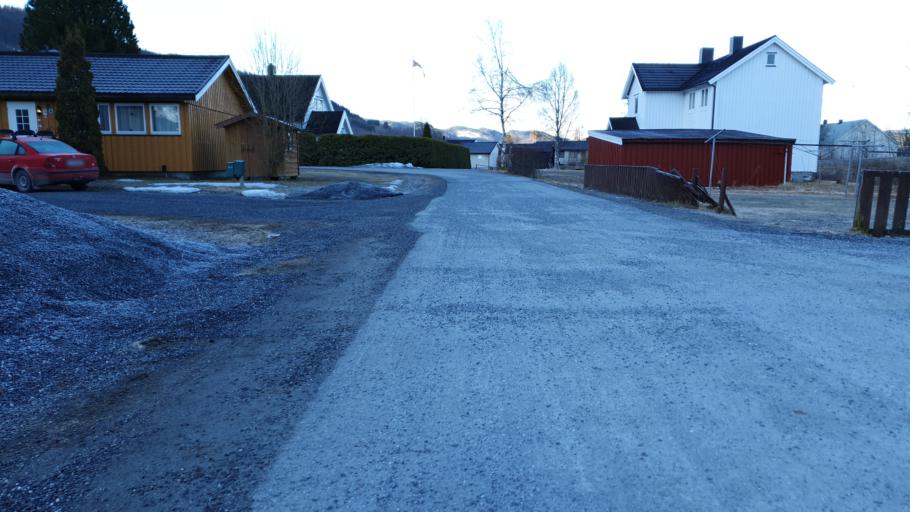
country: NO
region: Sor-Trondelag
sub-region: Orkdal
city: Orkanger
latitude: 63.2908
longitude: 9.8450
